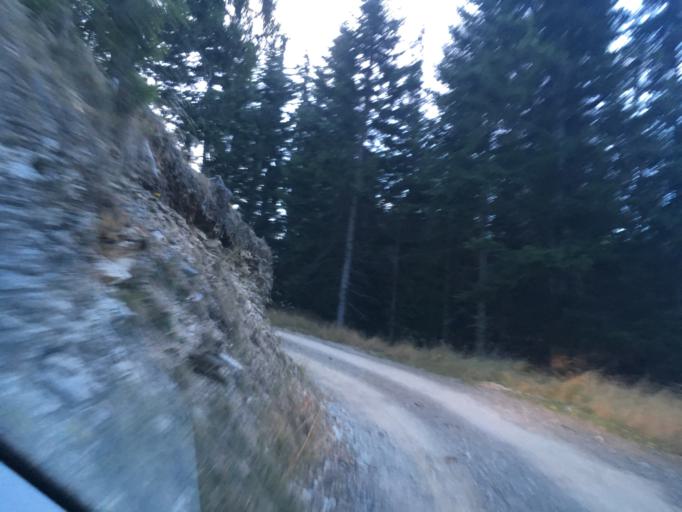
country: FR
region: Rhone-Alpes
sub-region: Departement de la Savoie
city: Modane
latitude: 45.2017
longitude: 6.6432
